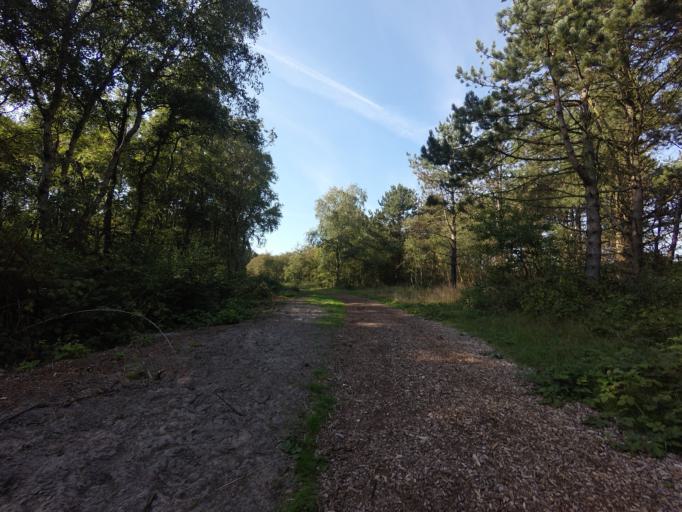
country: NL
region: Friesland
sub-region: Gemeente Schiermonnikoog
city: Schiermonnikoog
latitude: 53.4887
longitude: 6.1741
